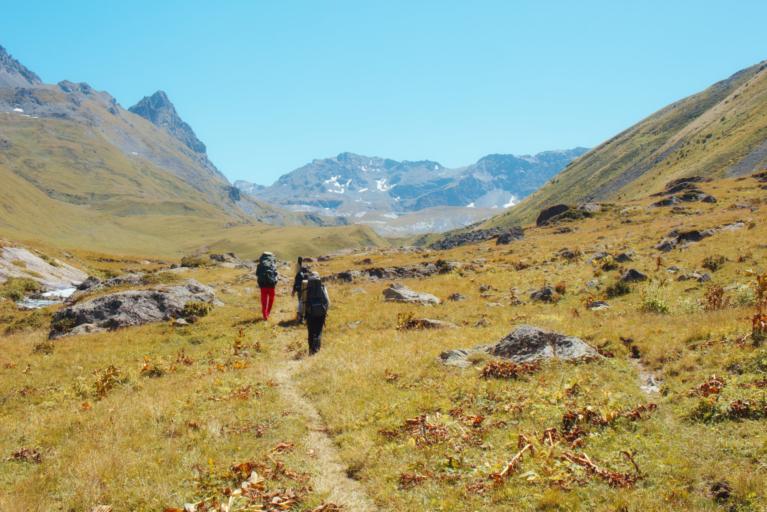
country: RU
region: Karachayevo-Cherkesiya
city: Mednogorskiy
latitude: 43.6294
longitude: 41.1431
